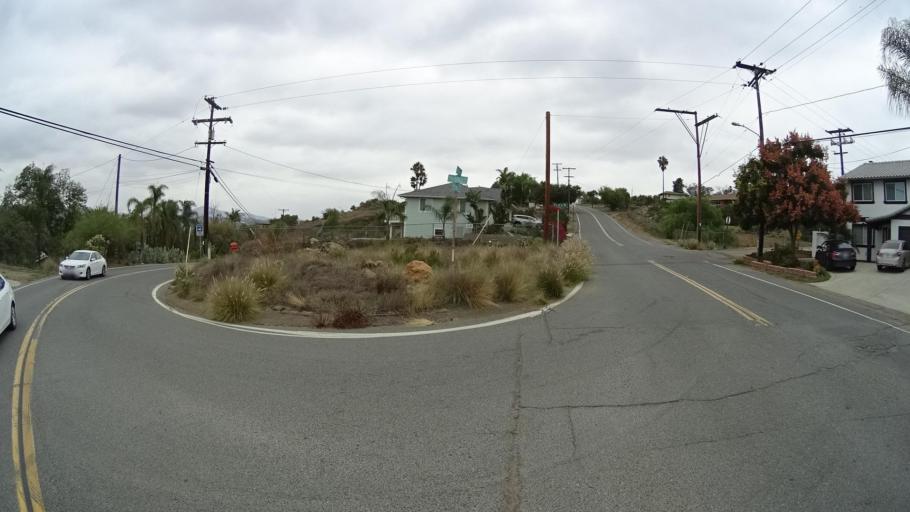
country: US
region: California
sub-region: San Diego County
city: Spring Valley
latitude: 32.7292
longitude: -116.9970
